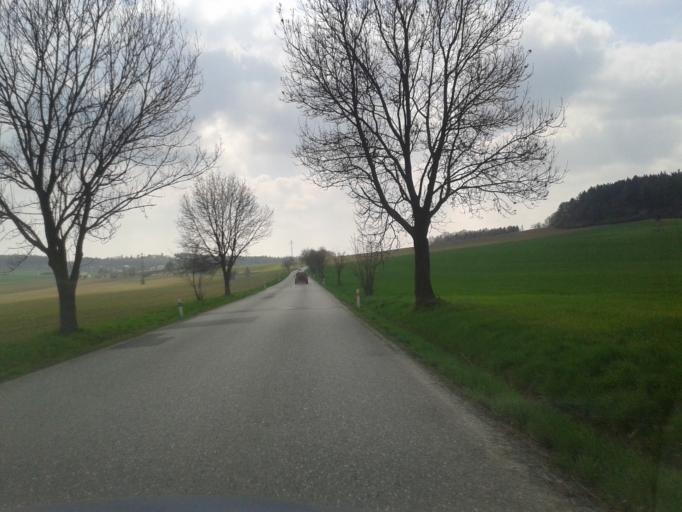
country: CZ
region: Central Bohemia
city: Chynava
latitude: 50.0065
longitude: 14.0917
